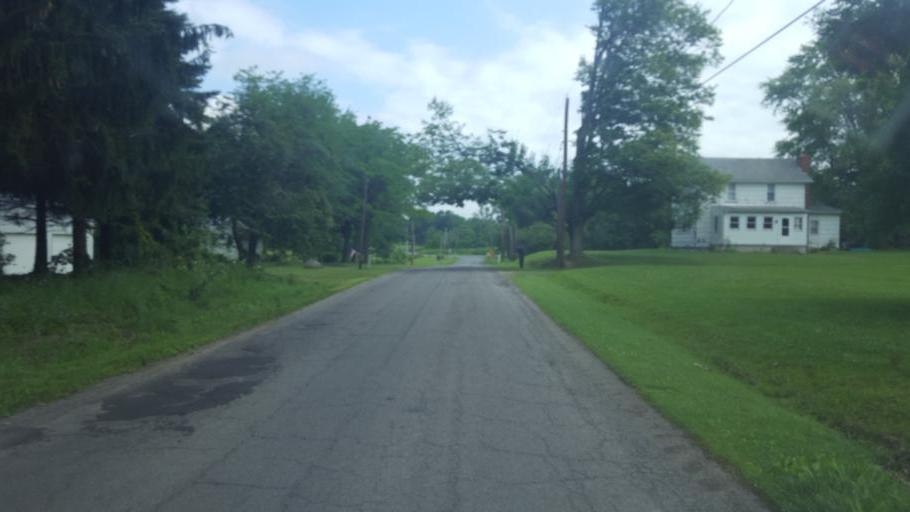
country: US
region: Ohio
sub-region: Crawford County
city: Galion
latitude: 40.7101
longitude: -82.7834
